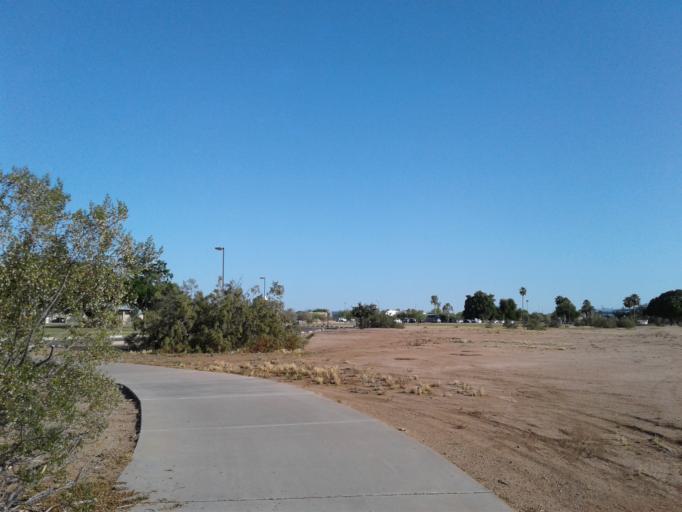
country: US
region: Arizona
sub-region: Maricopa County
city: Paradise Valley
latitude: 33.6493
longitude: -111.9974
